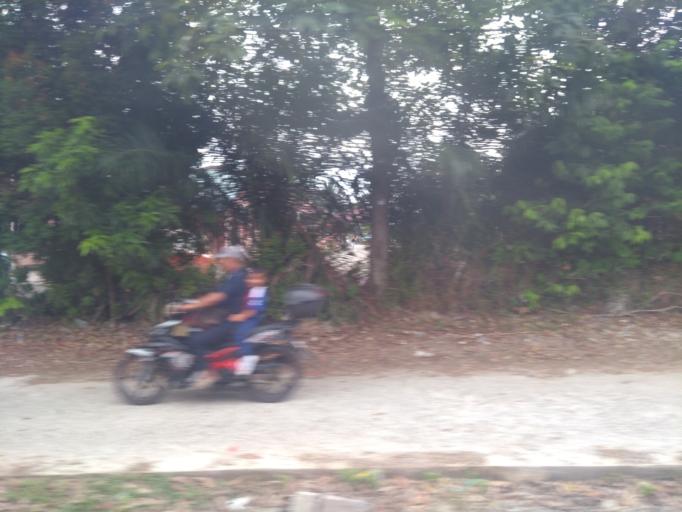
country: MY
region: Johor
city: Johor Bahru
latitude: 1.4931
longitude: 103.7061
